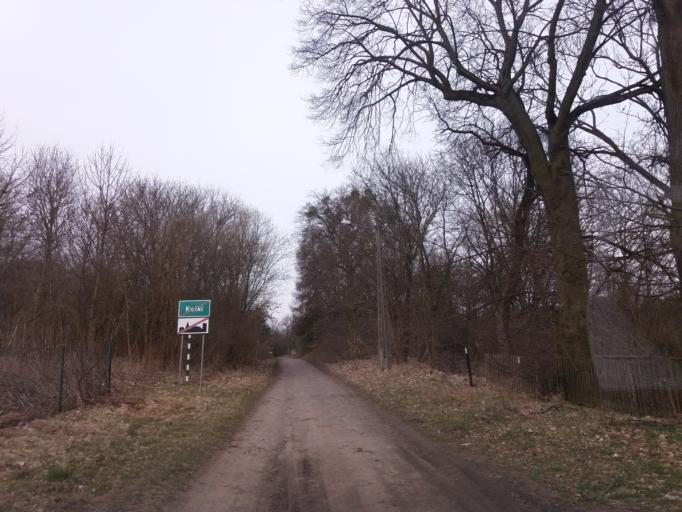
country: PL
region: West Pomeranian Voivodeship
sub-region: Powiat choszczenski
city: Bierzwnik
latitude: 53.1461
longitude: 15.6228
